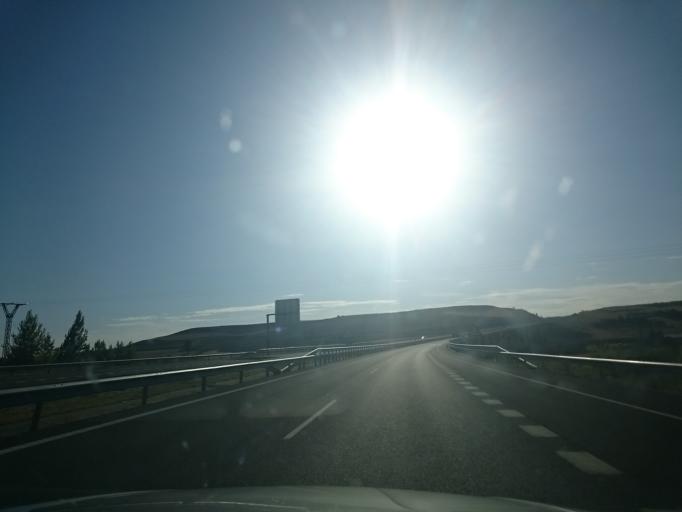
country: ES
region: Castille and Leon
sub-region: Provincia de Burgos
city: Villanueva de Argano
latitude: 42.3750
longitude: -3.9265
